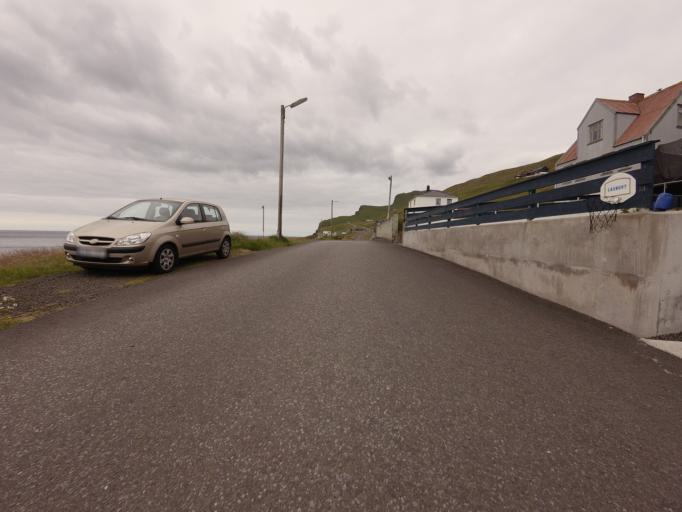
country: FO
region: Suduroy
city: Vagur
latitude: 61.4053
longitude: -6.7212
